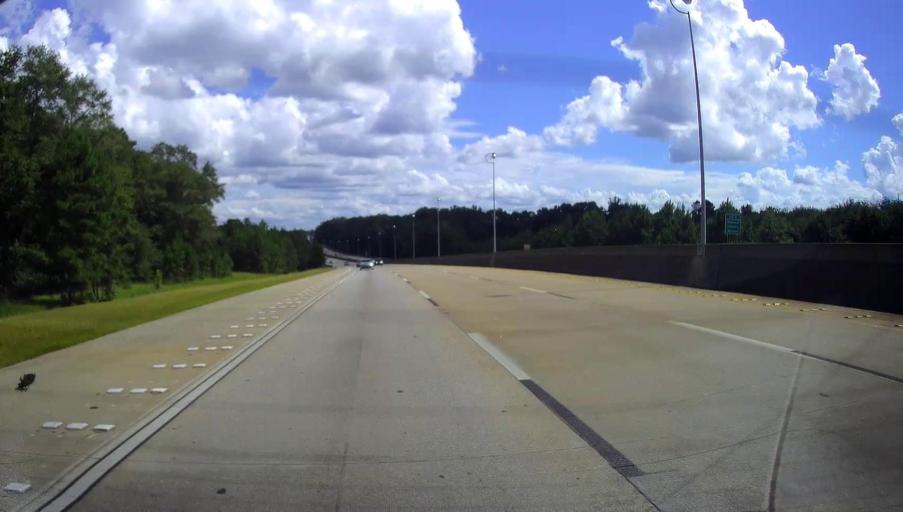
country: US
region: Georgia
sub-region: Muscogee County
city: Columbus
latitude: 32.4150
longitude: -84.9271
